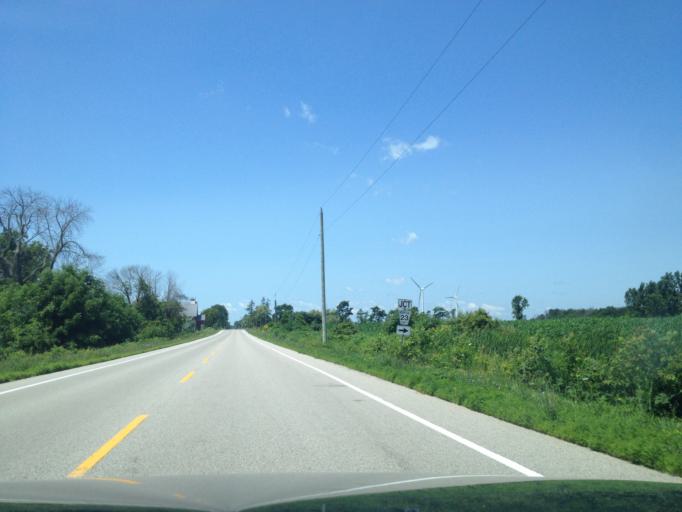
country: CA
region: Ontario
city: Norfolk County
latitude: 42.5784
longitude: -80.5616
